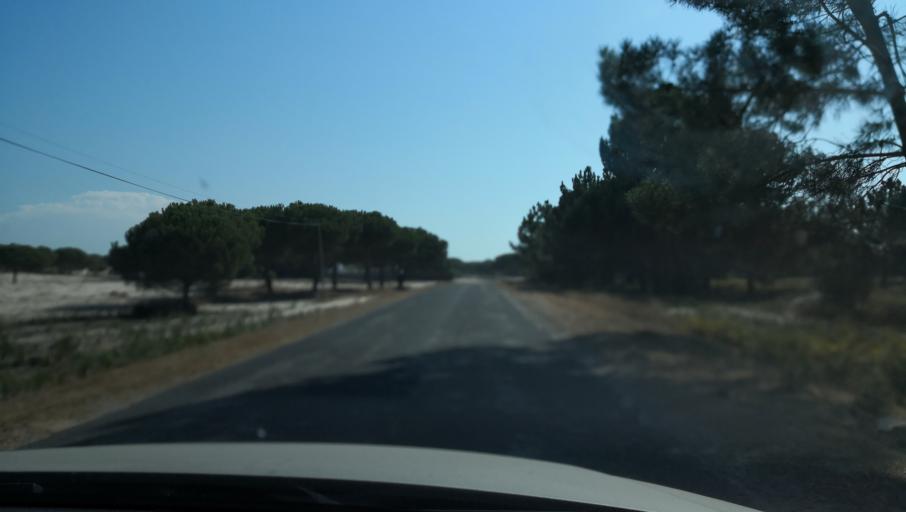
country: PT
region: Setubal
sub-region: Setubal
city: Setubal
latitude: 38.4042
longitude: -8.7546
